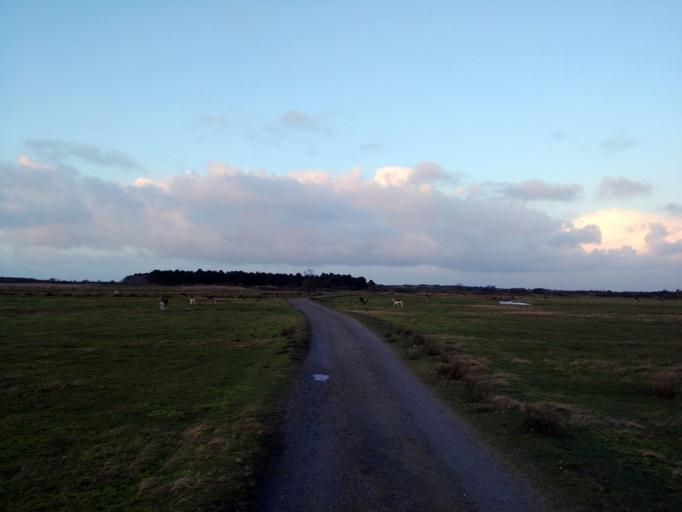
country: NL
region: South Holland
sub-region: Gemeente Noordwijkerhout
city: Noordwijkerhout
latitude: 52.3094
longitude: 4.5120
